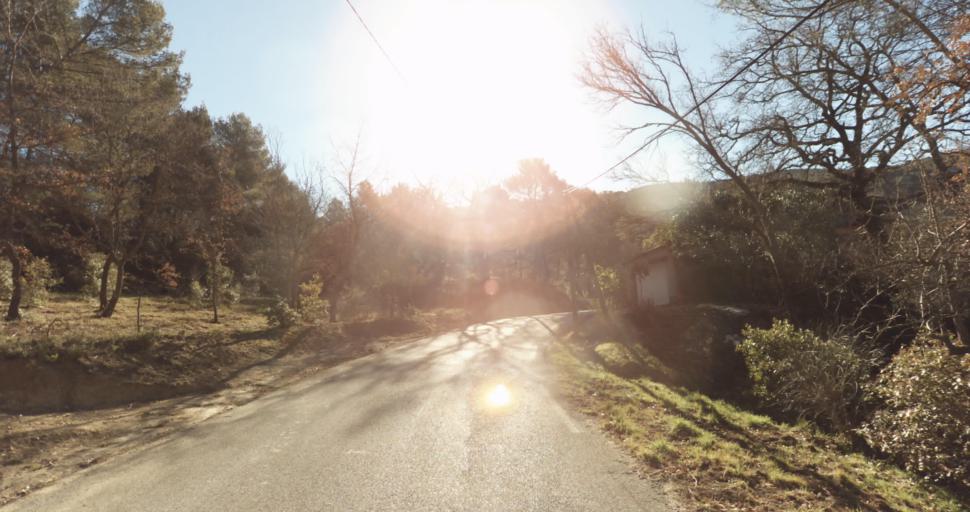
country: FR
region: Provence-Alpes-Cote d'Azur
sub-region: Departement des Bouches-du-Rhone
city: Peypin
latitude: 43.3651
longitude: 5.5673
